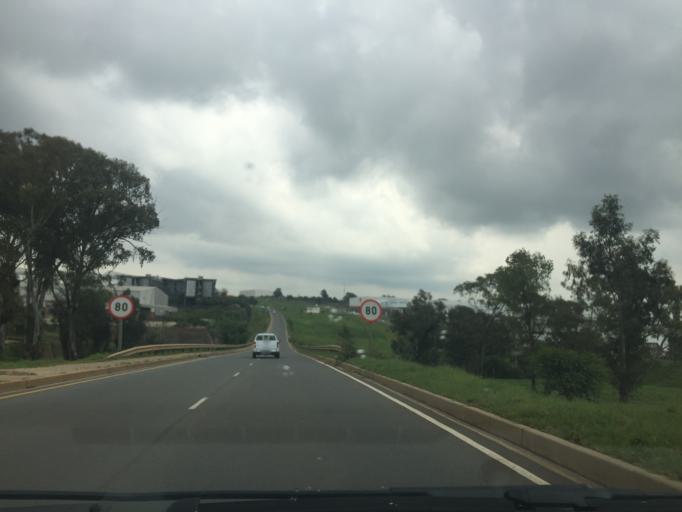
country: ZA
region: Gauteng
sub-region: City of Johannesburg Metropolitan Municipality
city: Modderfontein
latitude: -26.1067
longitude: 28.1438
